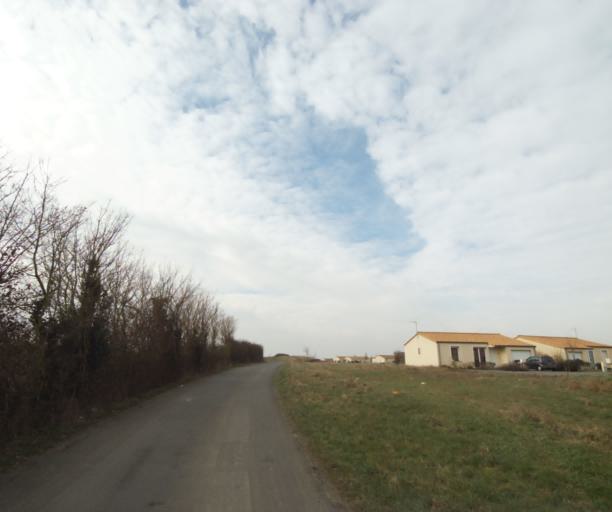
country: FR
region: Poitou-Charentes
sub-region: Departement des Deux-Sevres
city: Aiffres
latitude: 46.3109
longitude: -0.4326
